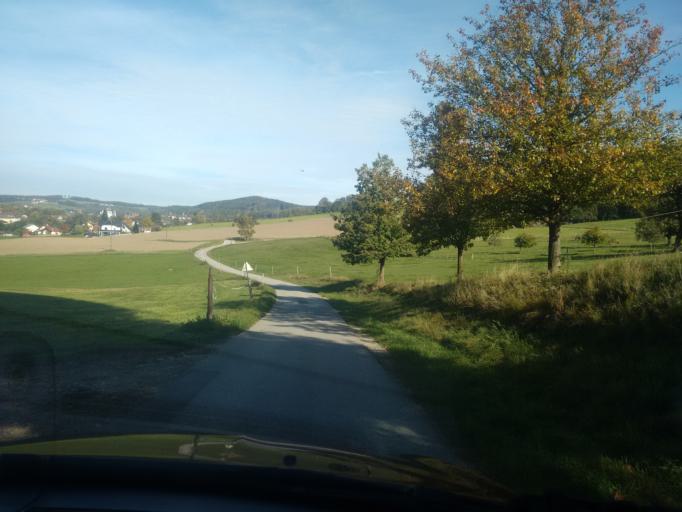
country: AT
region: Upper Austria
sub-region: Politischer Bezirk Vocklabruck
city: Zell am Pettenfirst
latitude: 48.0784
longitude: 13.5718
